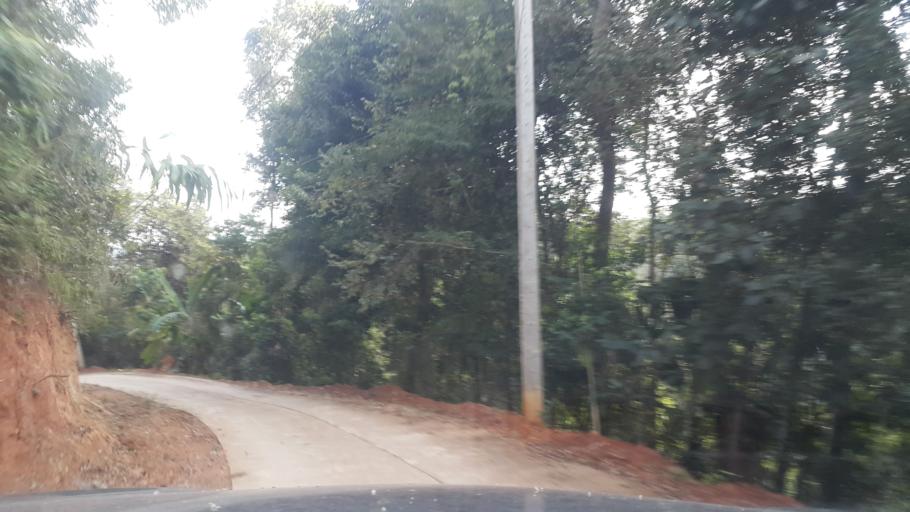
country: TH
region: Chiang Mai
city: Samoeng
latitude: 19.0058
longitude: 98.6512
